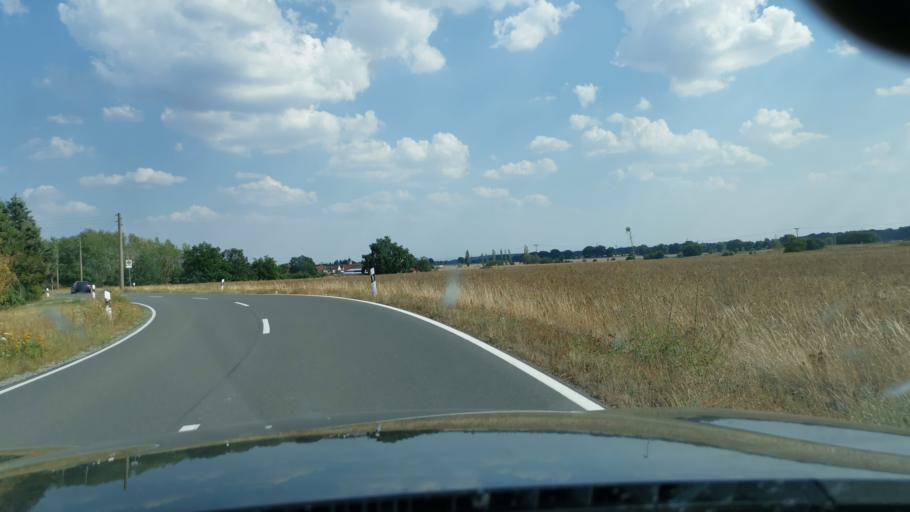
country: DE
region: Saxony
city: Bad Duben
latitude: 51.5647
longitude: 12.5628
